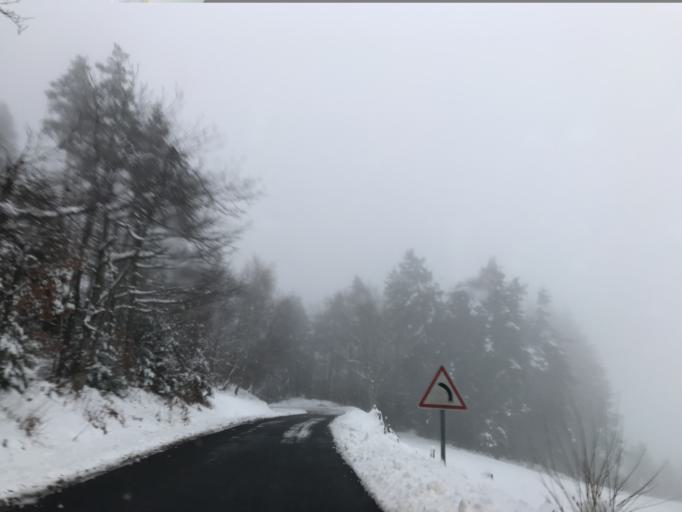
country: FR
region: Auvergne
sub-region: Departement du Puy-de-Dome
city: Celles-sur-Durolle
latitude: 45.7520
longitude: 3.6639
